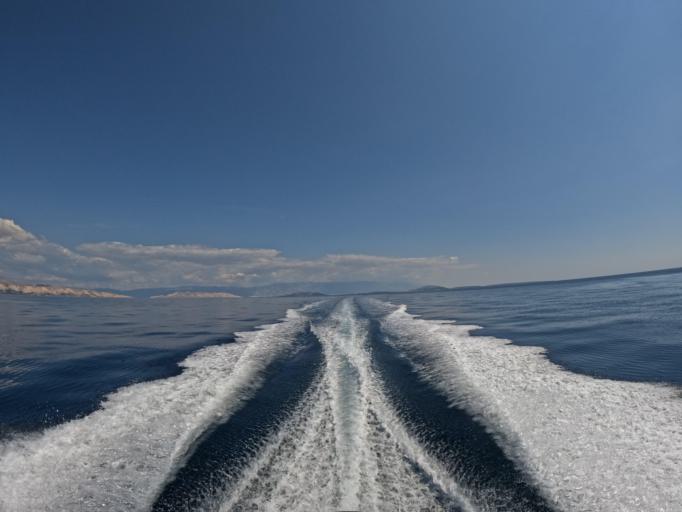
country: HR
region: Primorsko-Goranska
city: Punat
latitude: 44.9144
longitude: 14.5827
